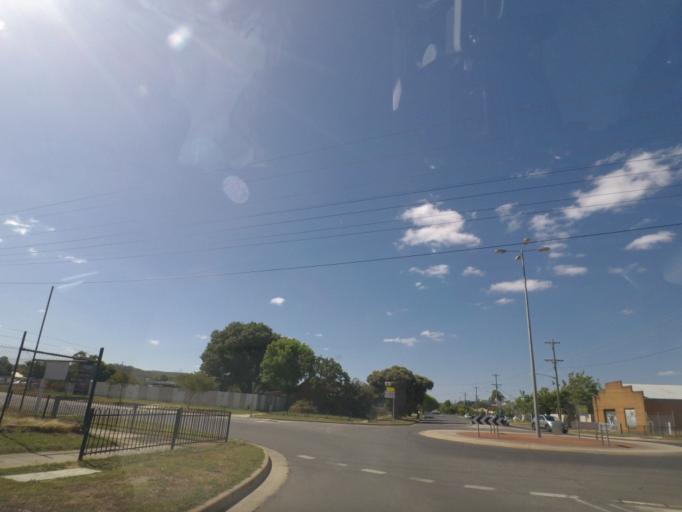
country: AU
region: New South Wales
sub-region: Albury Municipality
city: South Albury
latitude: -36.0912
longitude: 146.9136
